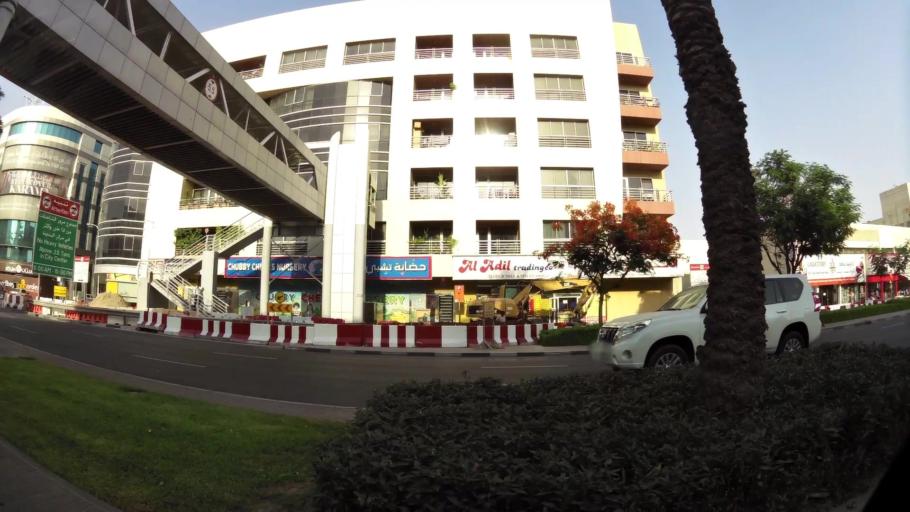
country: AE
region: Ash Shariqah
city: Sharjah
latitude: 25.2468
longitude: 55.3081
